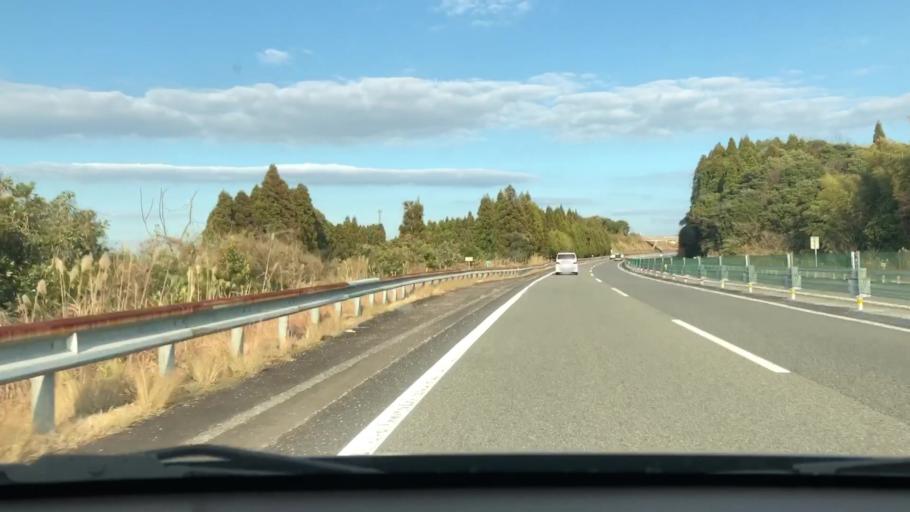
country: JP
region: Miyazaki
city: Miyazaki-shi
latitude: 31.8295
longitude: 131.3137
